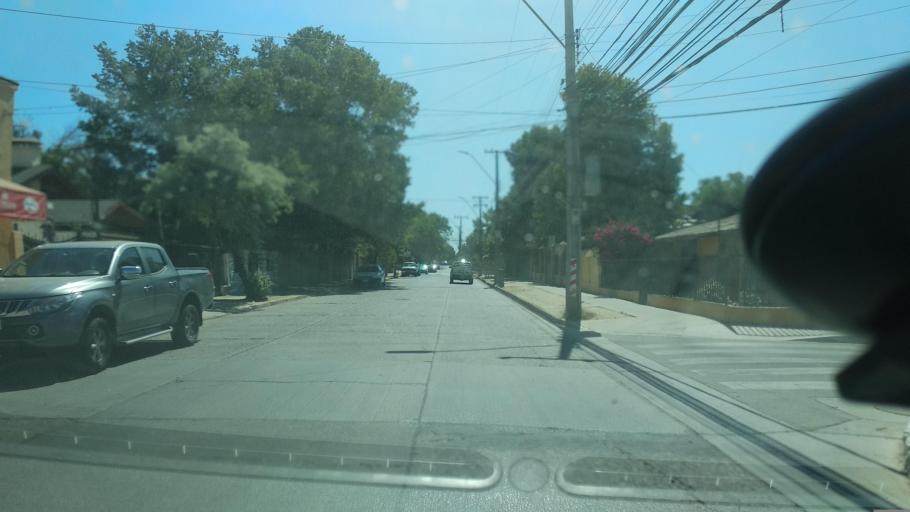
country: CL
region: Valparaiso
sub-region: Provincia de Marga Marga
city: Villa Alemana
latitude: -33.0462
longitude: -71.3670
